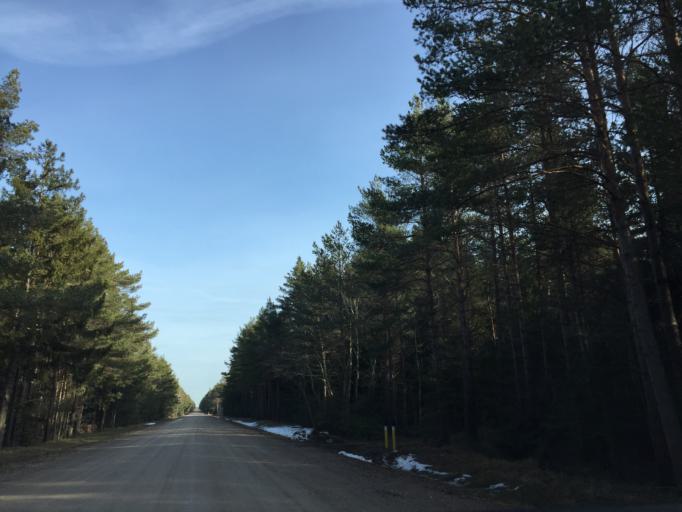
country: EE
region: Saare
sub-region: Kuressaare linn
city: Kuressaare
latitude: 58.3066
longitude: 21.9699
